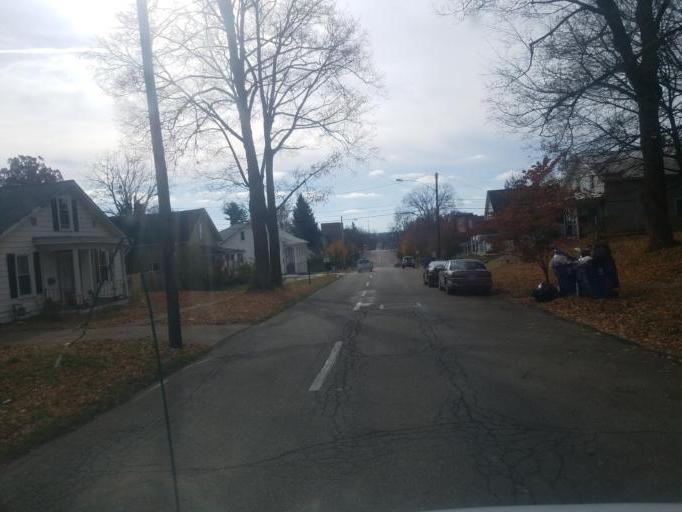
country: US
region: Ohio
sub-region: Knox County
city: Mount Vernon
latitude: 40.3990
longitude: -82.4862
